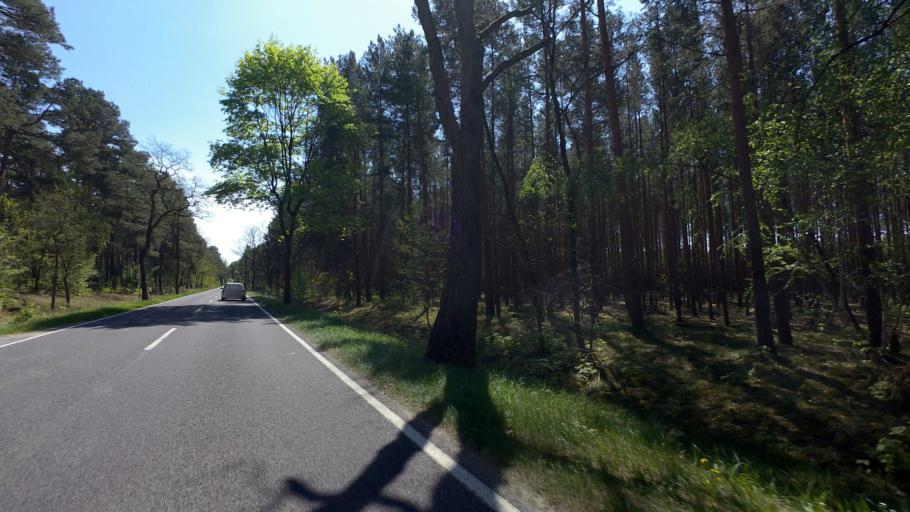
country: DE
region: Brandenburg
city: Gross Koris
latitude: 52.1793
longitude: 13.7120
